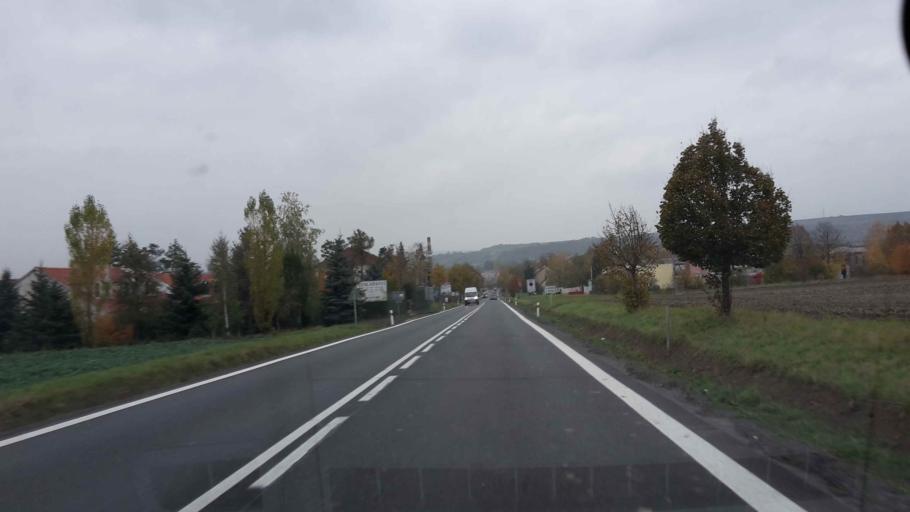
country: CZ
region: South Moravian
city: Slavkov u Brna
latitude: 49.1401
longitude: 16.8801
